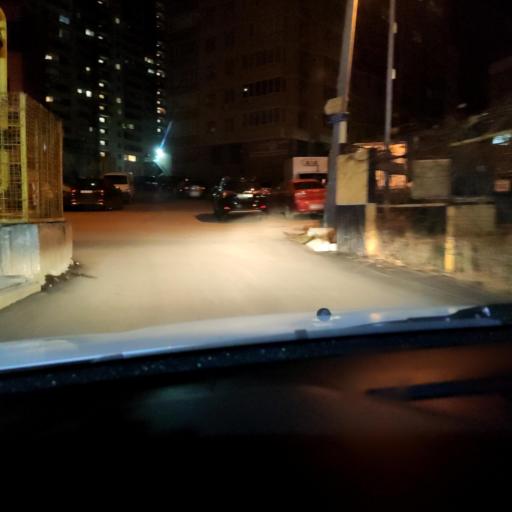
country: RU
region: Samara
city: Samara
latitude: 53.2377
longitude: 50.1798
